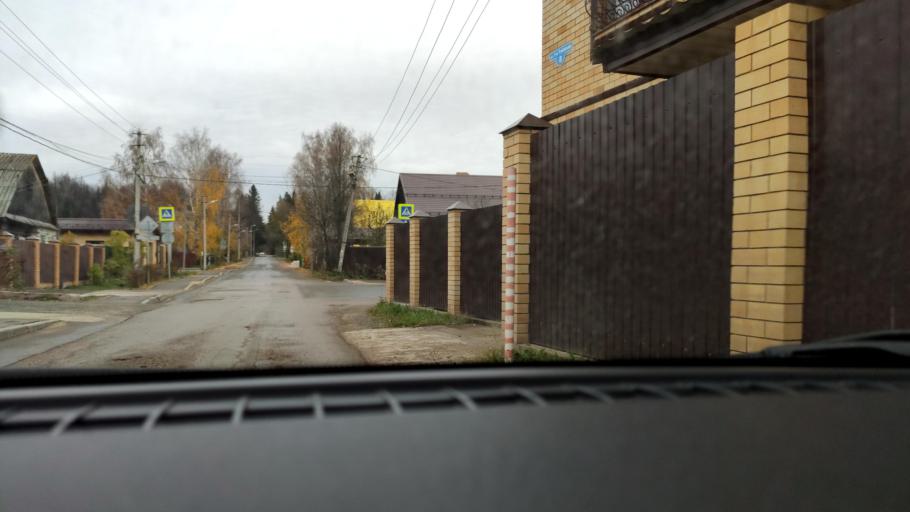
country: RU
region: Perm
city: Froly
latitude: 57.9505
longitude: 56.2995
